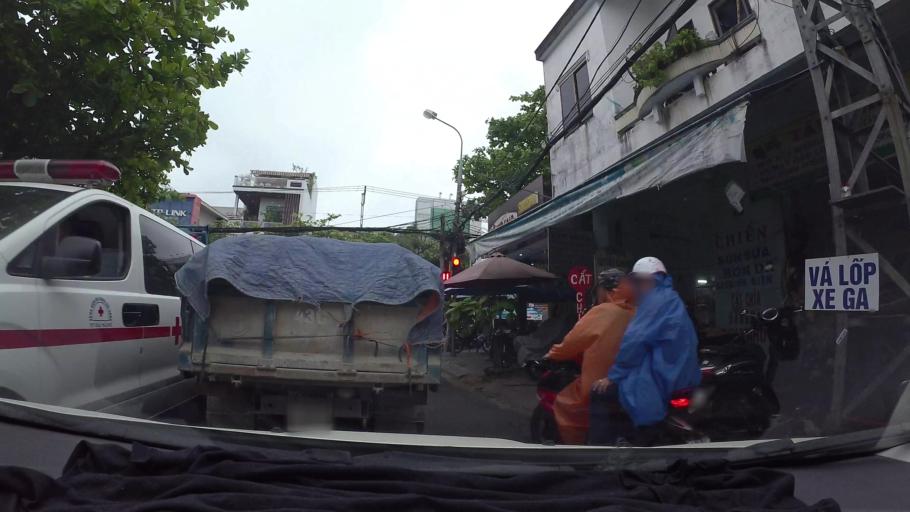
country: VN
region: Da Nang
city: Da Nang
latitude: 16.0758
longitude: 108.2148
